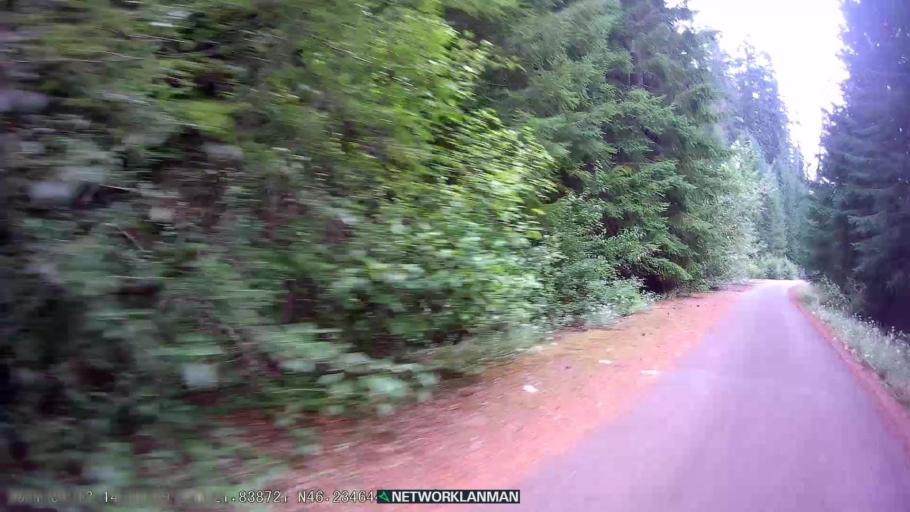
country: US
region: Washington
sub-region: Skamania County
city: Carson
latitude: 46.2346
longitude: -121.8386
